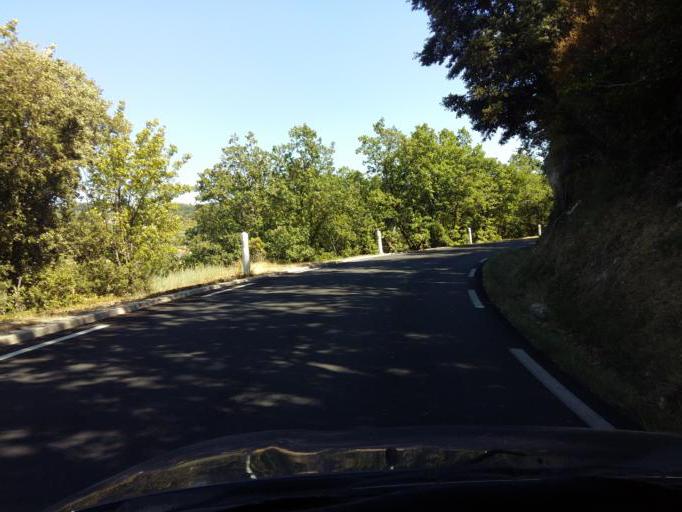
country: FR
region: Provence-Alpes-Cote d'Azur
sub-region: Departement du Vaucluse
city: Venasque
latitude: 44.0105
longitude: 5.1347
